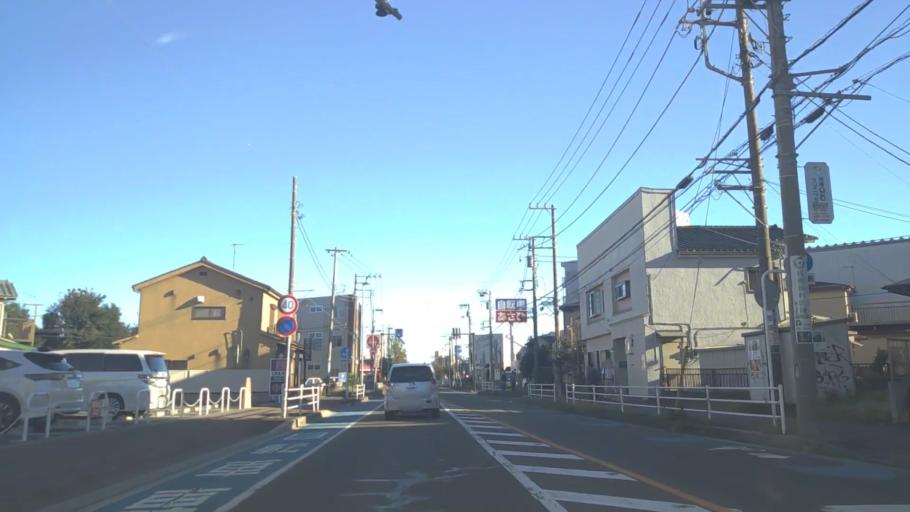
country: JP
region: Kanagawa
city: Chigasaki
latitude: 35.3429
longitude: 139.3984
